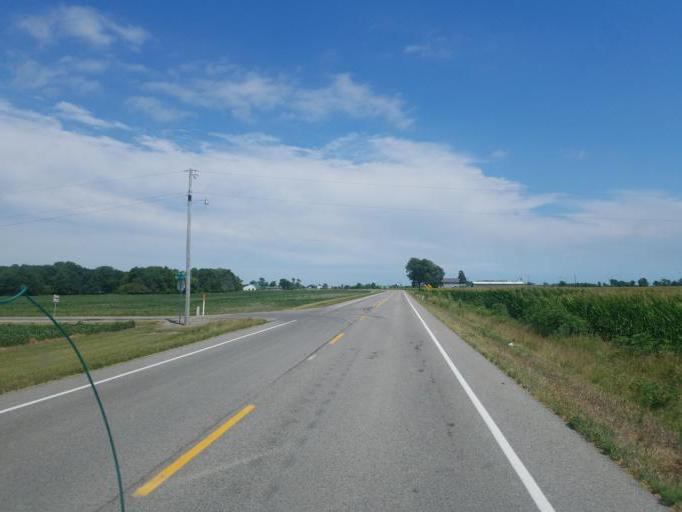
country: US
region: Indiana
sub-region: Allen County
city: Woodburn
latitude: 41.1544
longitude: -84.8397
